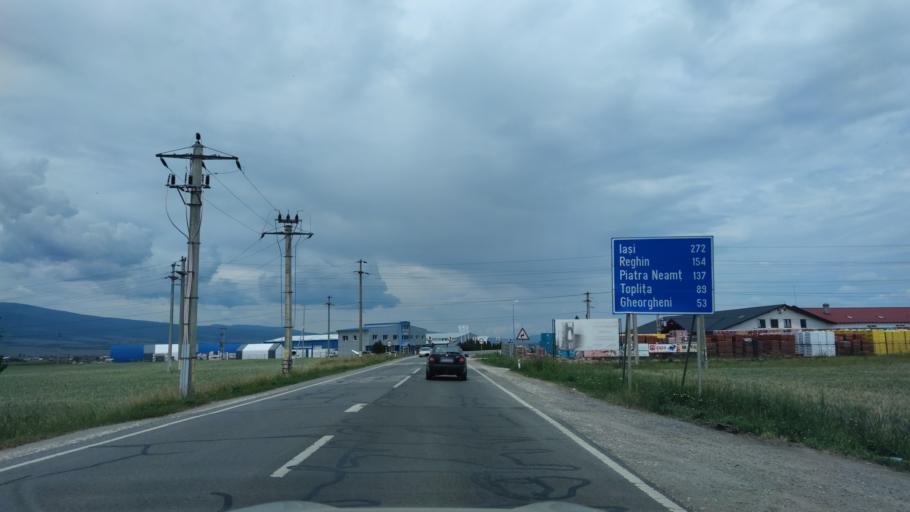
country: RO
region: Harghita
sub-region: Municipiul Miercurea Ciuc
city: Miercurea-Ciuc
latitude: 46.3830
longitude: 25.7990
